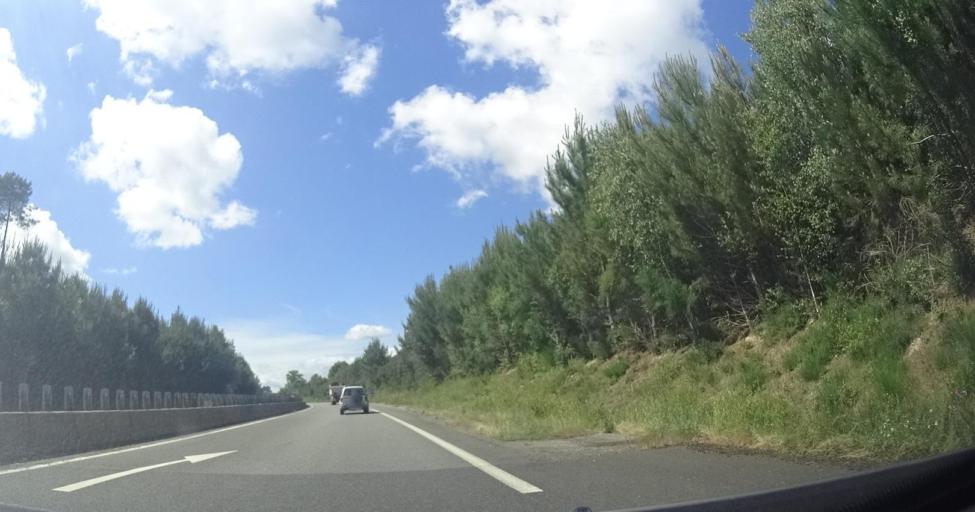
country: FR
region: Brittany
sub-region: Departement du Morbihan
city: Pluherlin
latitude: 47.6733
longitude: -2.3640
